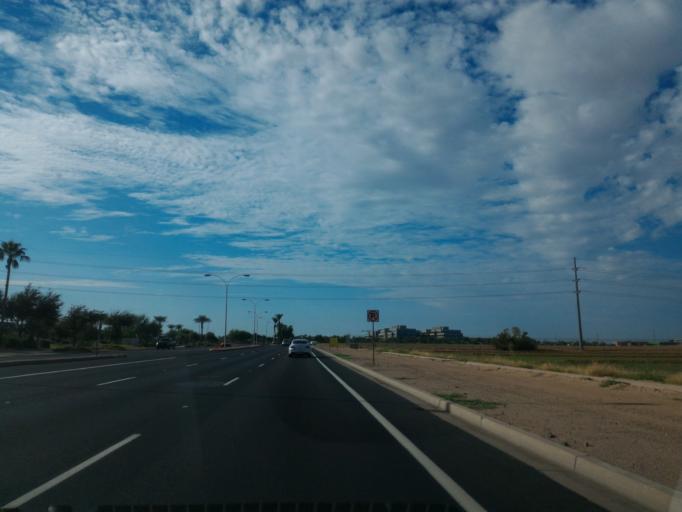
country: US
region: Arizona
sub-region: Maricopa County
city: Chandler
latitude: 33.2734
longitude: -111.8892
